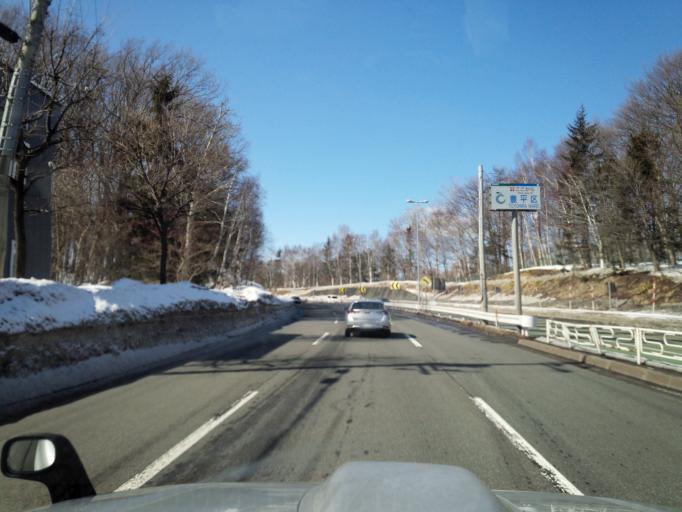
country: JP
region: Hokkaido
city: Sapporo
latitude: 43.0042
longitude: 141.4261
